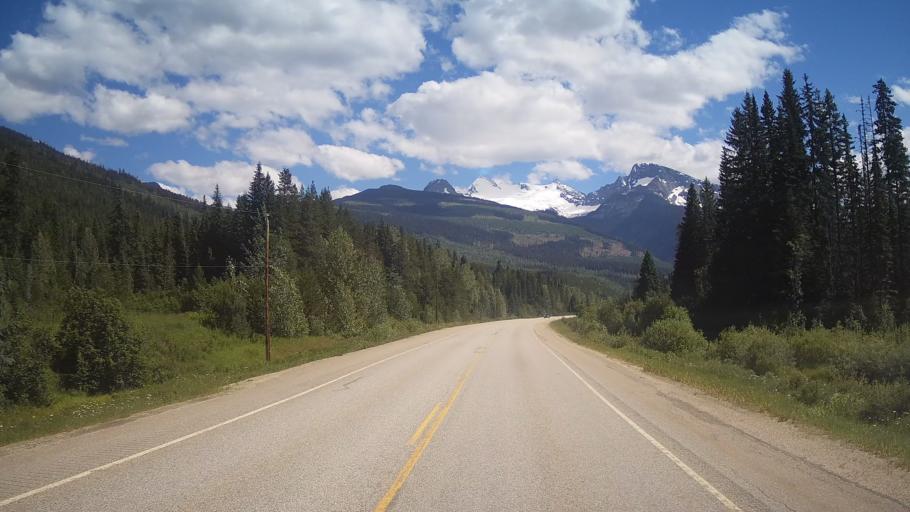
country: CA
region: Alberta
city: Jasper Park Lodge
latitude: 52.5959
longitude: -119.1030
